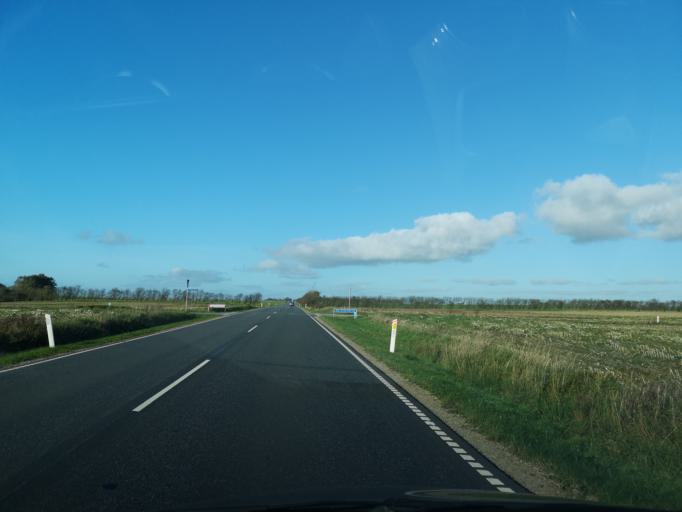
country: DK
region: South Denmark
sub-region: Varde Kommune
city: Varde
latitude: 55.7091
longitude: 8.4944
